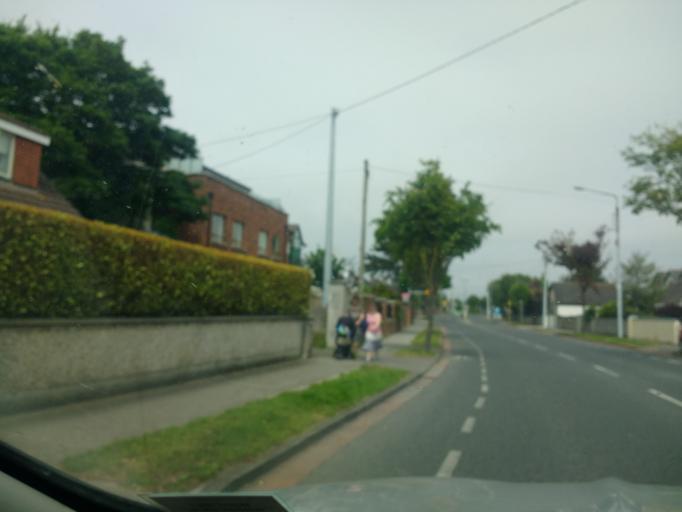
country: IE
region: Leinster
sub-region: Fingal County
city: Baldoyle
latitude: 53.3901
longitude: -6.1240
